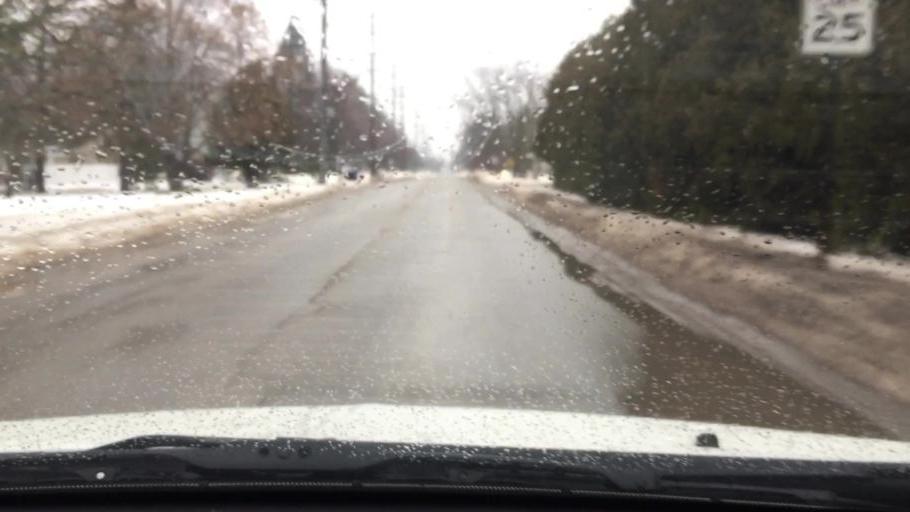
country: US
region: Michigan
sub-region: Charlevoix County
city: Charlevoix
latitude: 45.3063
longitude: -85.2555
